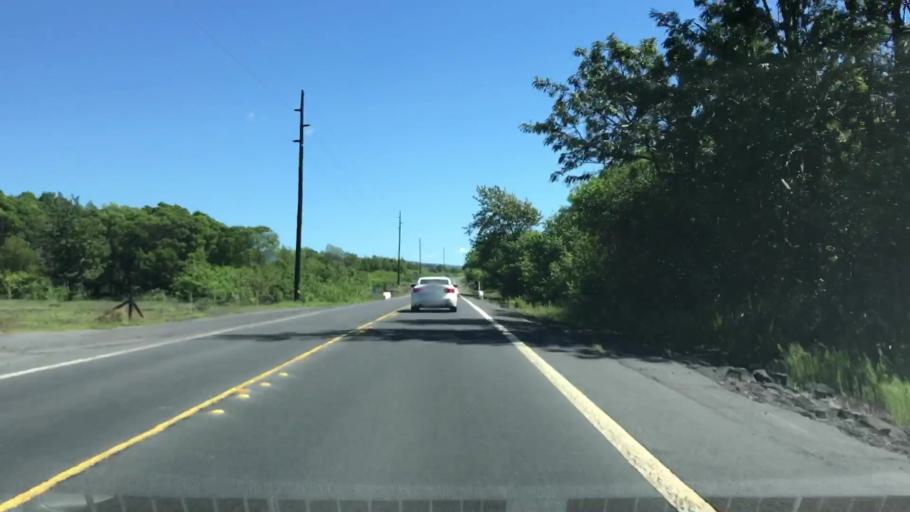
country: US
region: Hawaii
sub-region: Hawaii County
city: Pahala
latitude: 19.2680
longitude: -155.4355
